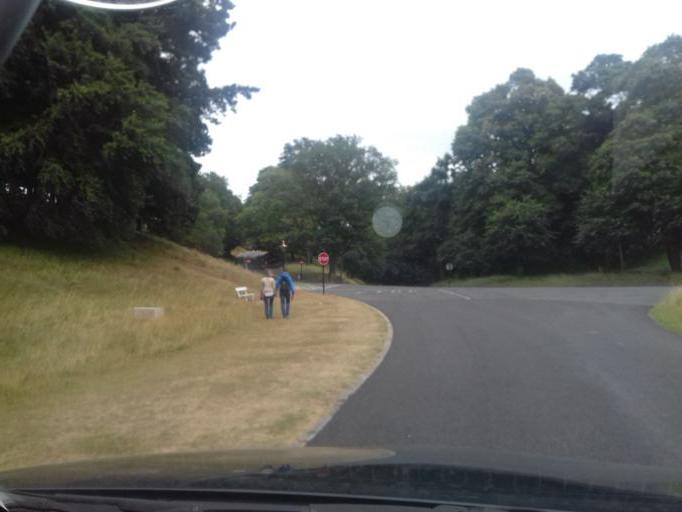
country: IE
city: Greenhills
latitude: 53.3491
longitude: -6.3139
